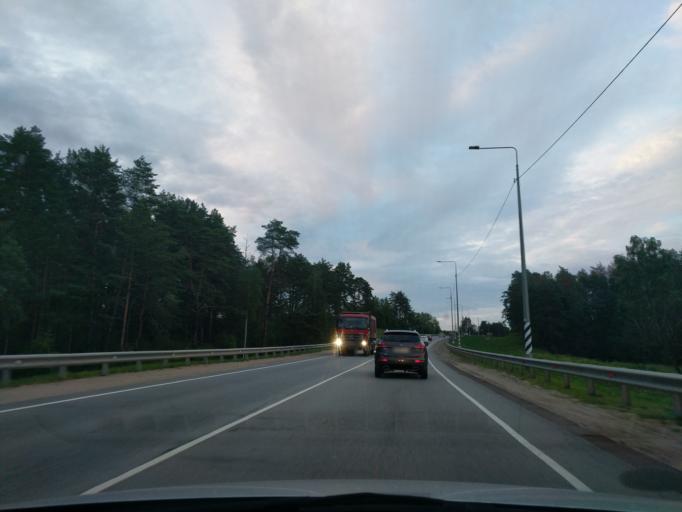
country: RU
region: Kaluga
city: Obninsk
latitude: 55.0453
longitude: 36.5513
